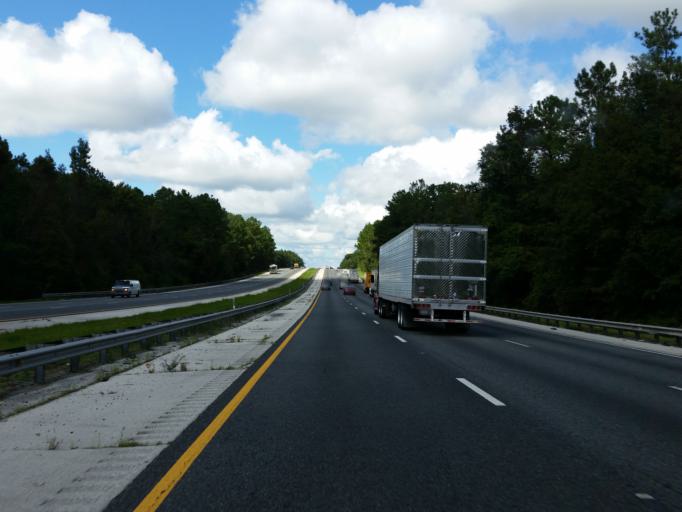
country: US
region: Florida
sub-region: Alachua County
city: Gainesville
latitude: 29.4758
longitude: -82.2803
